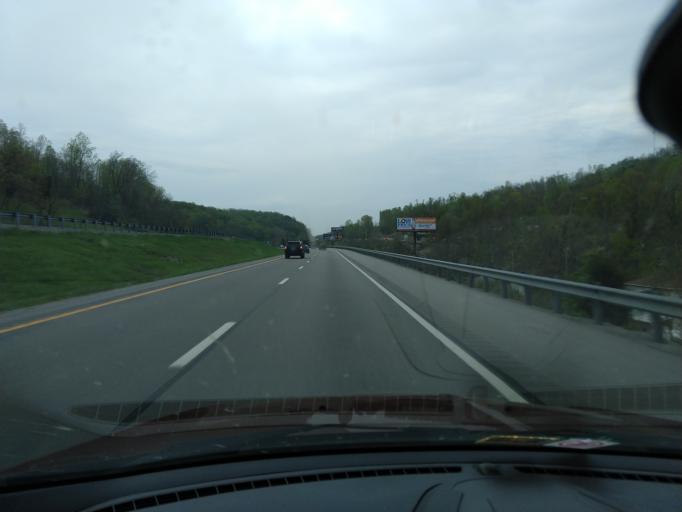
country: US
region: West Virginia
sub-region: Lewis County
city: Weston
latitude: 39.1327
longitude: -80.3789
